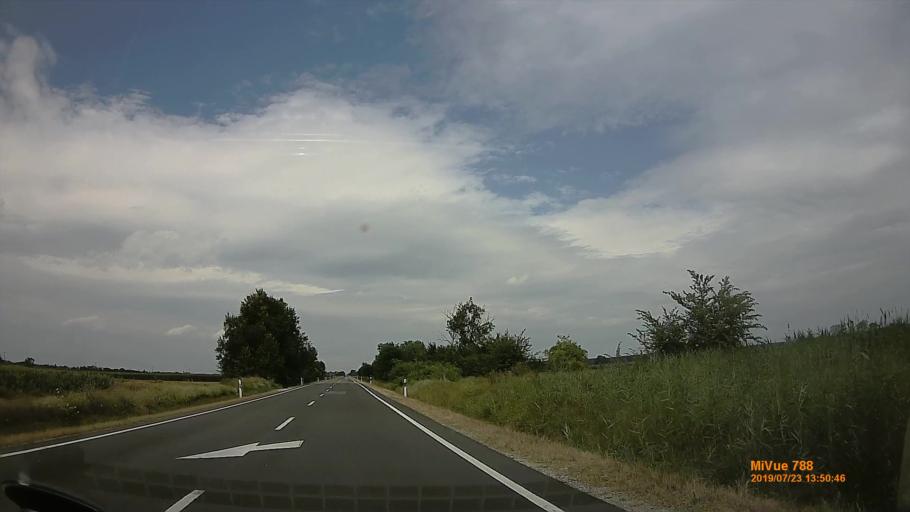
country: HU
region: Hajdu-Bihar
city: Polgar
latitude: 47.8790
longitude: 21.1455
